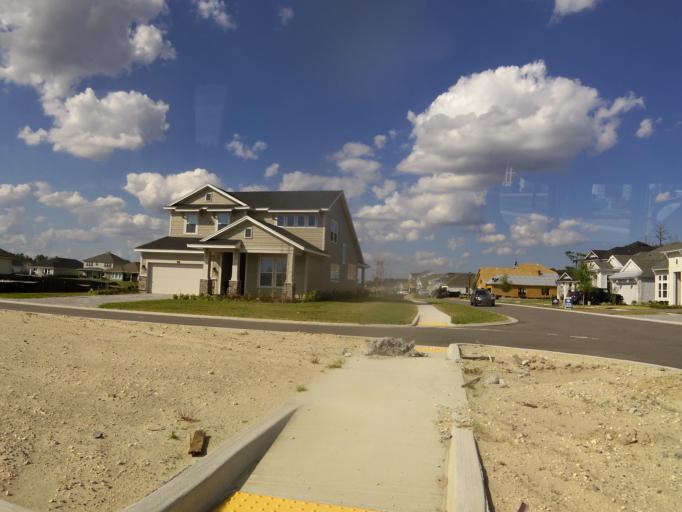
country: US
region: Florida
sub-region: Saint Johns County
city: Palm Valley
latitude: 30.1737
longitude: -81.5030
